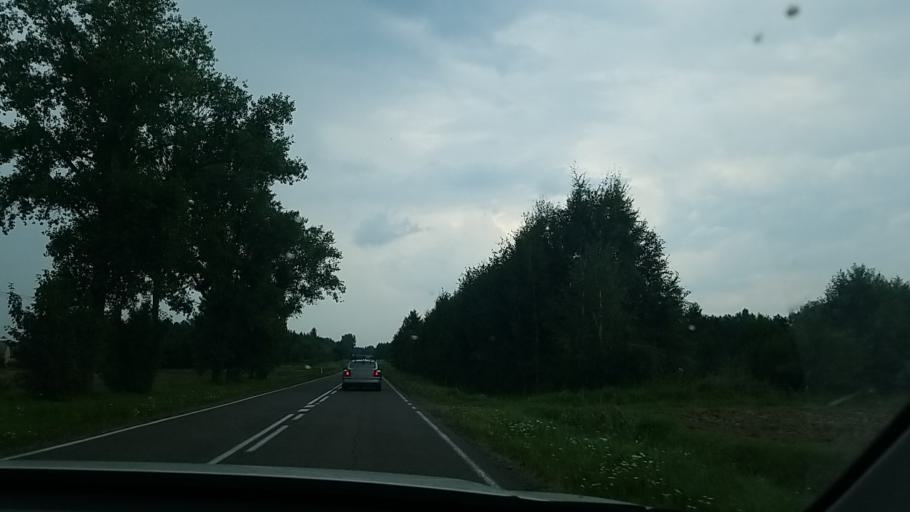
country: PL
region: Lublin Voivodeship
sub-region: Powiat leczynski
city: Cycow
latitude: 51.2778
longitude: 23.0984
